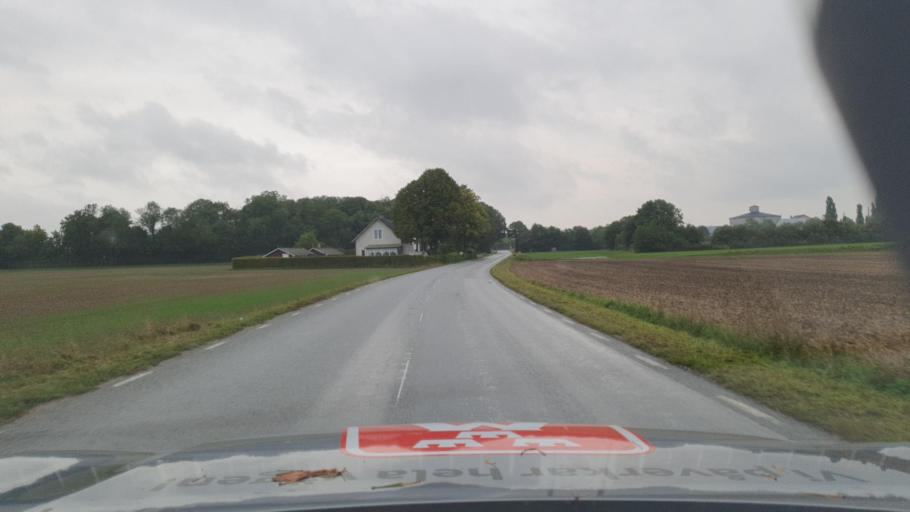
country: SE
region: Gotland
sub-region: Gotland
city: Visby
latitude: 57.5057
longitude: 18.4388
